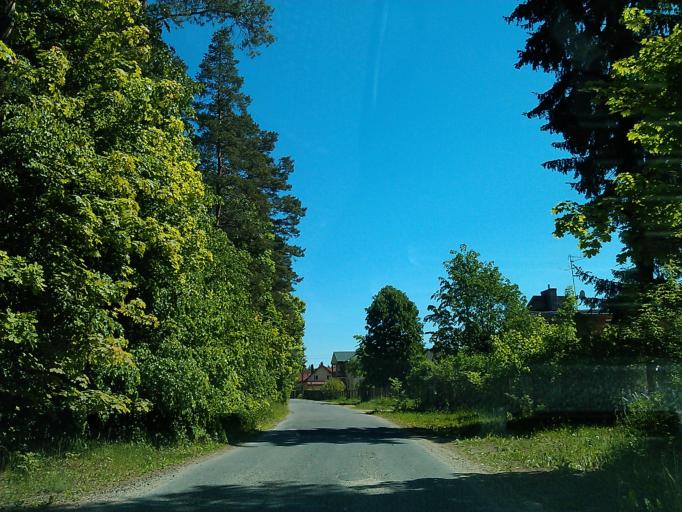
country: LV
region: Riga
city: Bergi
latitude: 56.9975
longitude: 24.3108
